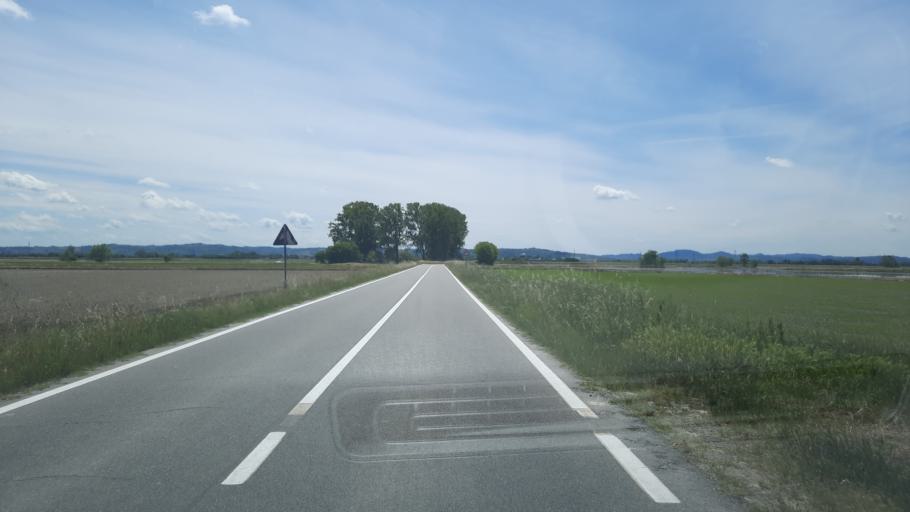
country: IT
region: Piedmont
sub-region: Provincia di Vercelli
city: Rive
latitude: 45.2042
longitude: 8.4143
